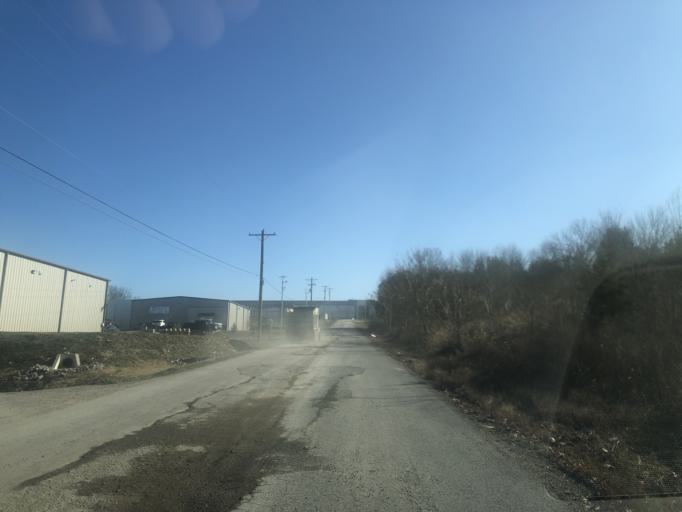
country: US
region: Tennessee
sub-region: Rutherford County
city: La Vergne
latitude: 36.0064
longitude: -86.5904
